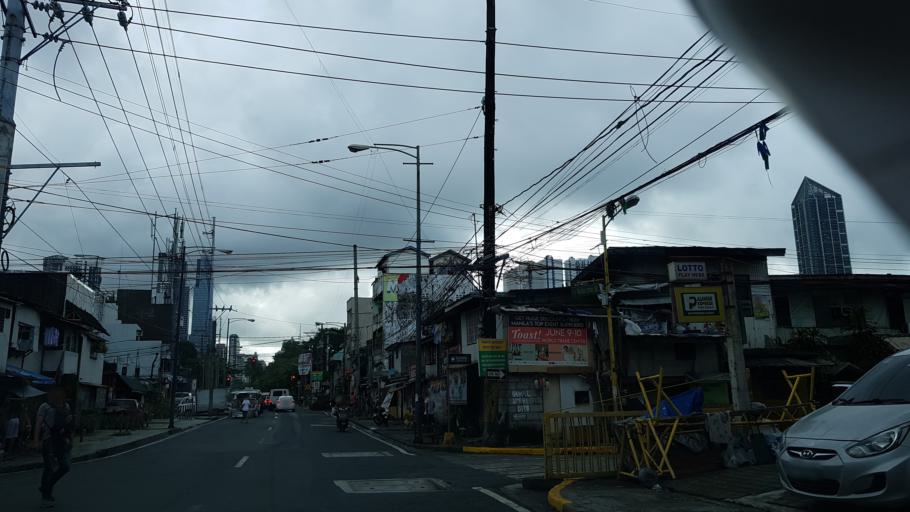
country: PH
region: Metro Manila
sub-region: Makati City
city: Makati City
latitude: 14.5692
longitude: 121.0169
